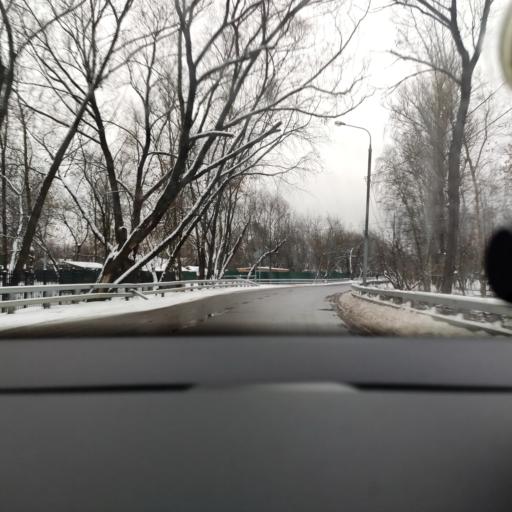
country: RU
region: Moscow
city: Zhulebino
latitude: 55.7176
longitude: 37.8479
